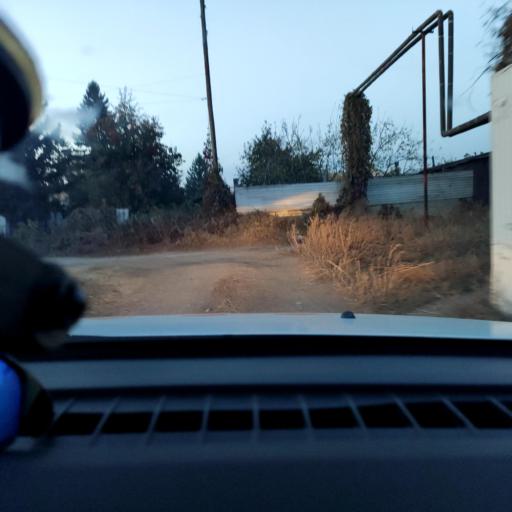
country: RU
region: Samara
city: Samara
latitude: 53.1508
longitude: 50.0892
